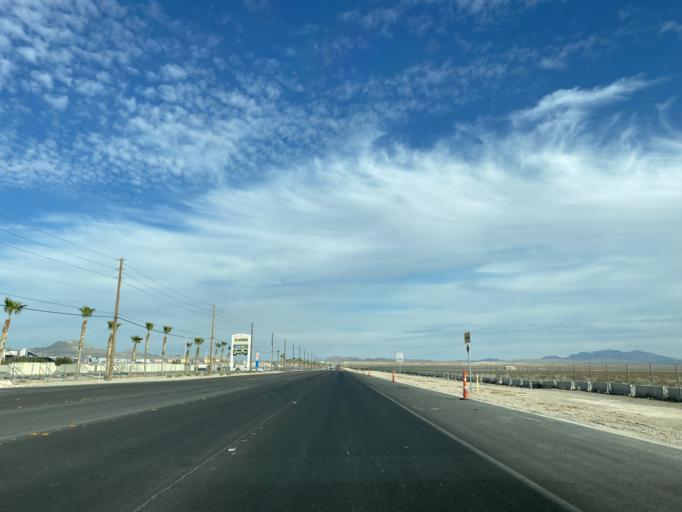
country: US
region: Nevada
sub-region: Clark County
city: Nellis Air Force Base
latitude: 36.2588
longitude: -115.0230
